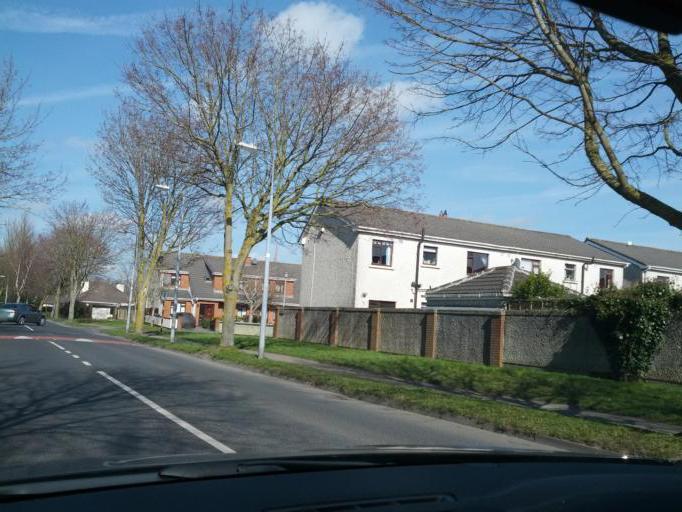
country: IE
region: Leinster
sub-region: Kildare
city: Maynooth
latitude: 53.3740
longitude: -6.5999
